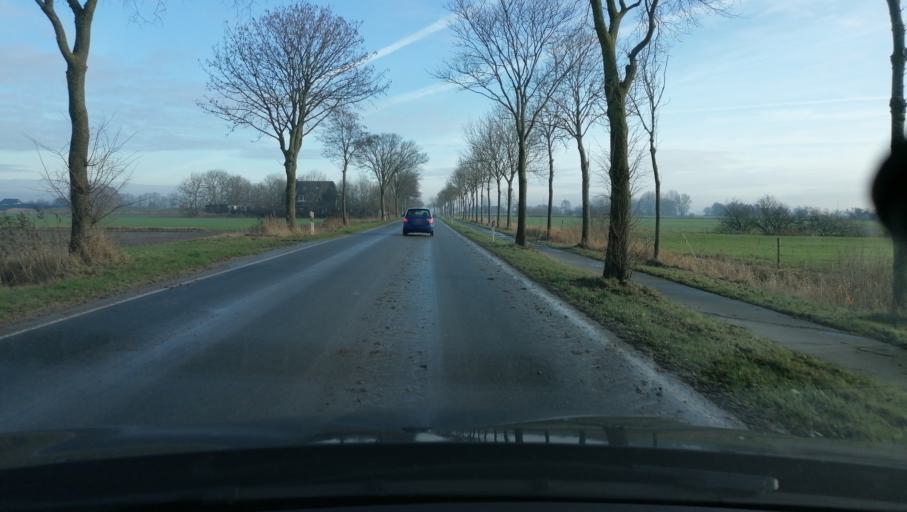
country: DE
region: Schleswig-Holstein
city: Wohrden
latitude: 54.1212
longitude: 9.0043
